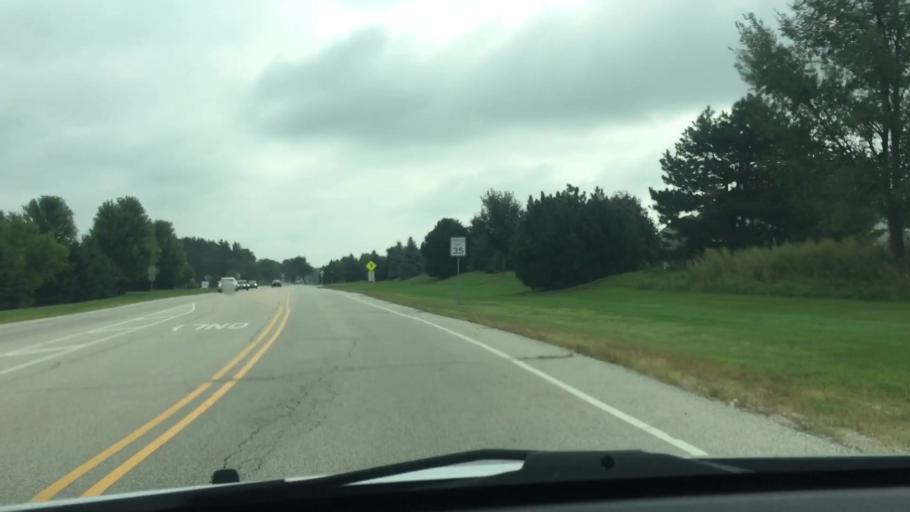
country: US
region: Wisconsin
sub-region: Waukesha County
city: Okauchee Lake
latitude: 43.0764
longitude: -88.4567
